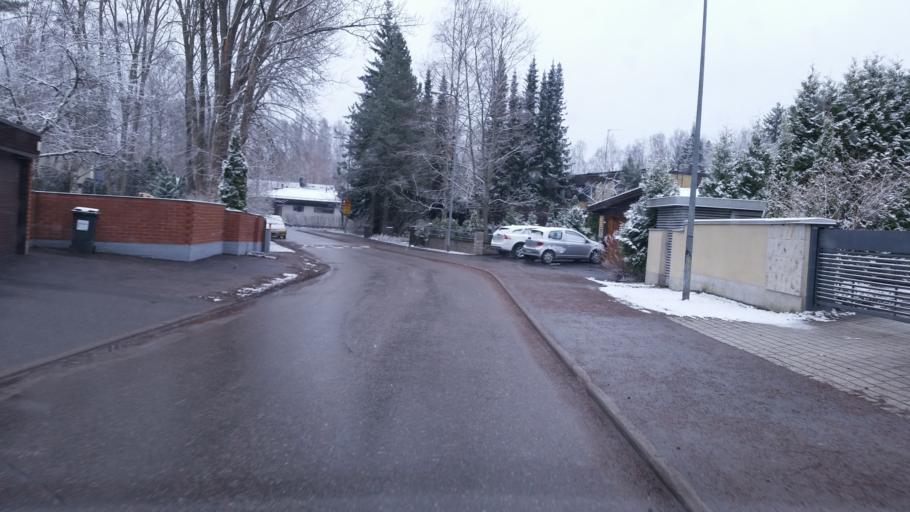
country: FI
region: Uusimaa
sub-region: Helsinki
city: Otaniemi
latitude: 60.1674
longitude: 24.8008
